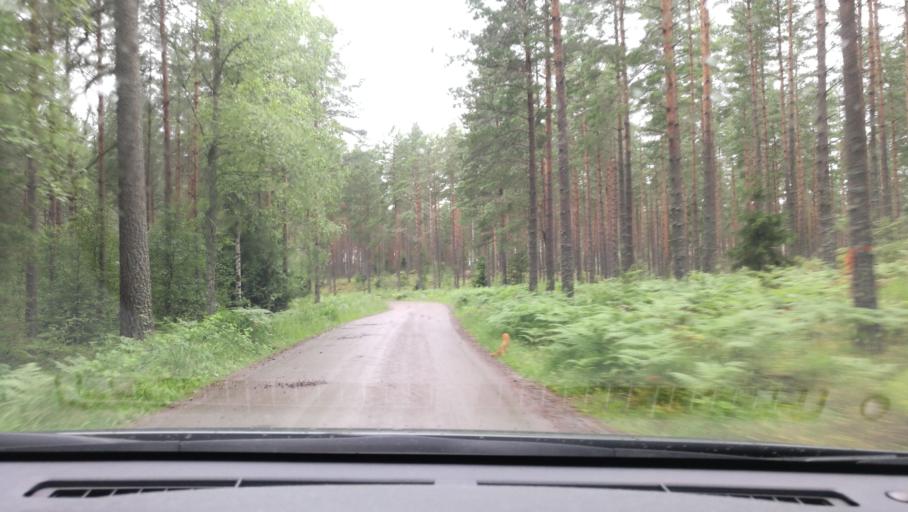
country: SE
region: OEstergoetland
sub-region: Norrkopings Kommun
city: Svartinge
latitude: 58.7585
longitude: 15.9735
